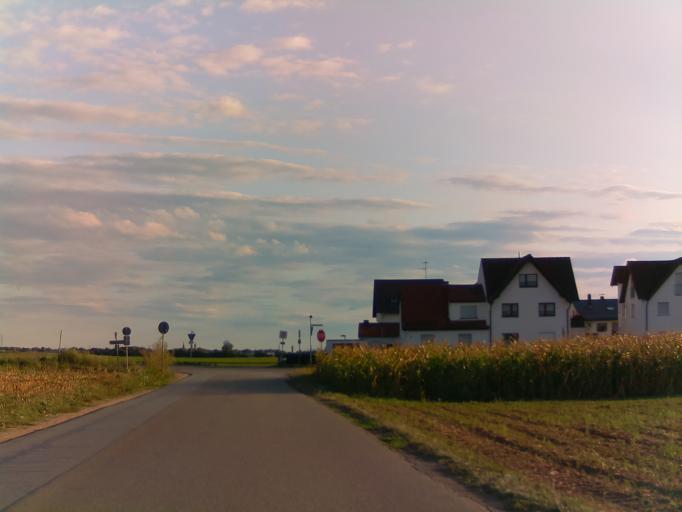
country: DE
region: Baden-Wuerttemberg
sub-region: Karlsruhe Region
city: Heddesheim
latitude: 49.5028
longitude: 8.6186
